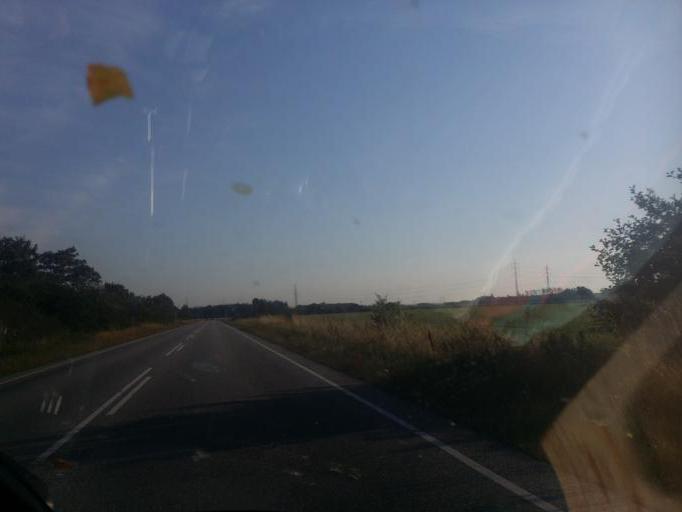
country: DK
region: South Denmark
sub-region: Tonder Kommune
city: Sherrebek
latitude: 55.0522
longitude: 8.8314
